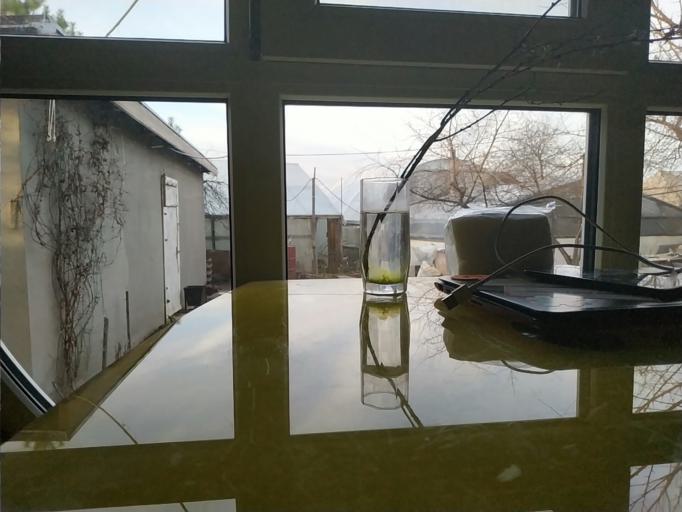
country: RU
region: Republic of Karelia
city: Suoyarvi
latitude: 62.2569
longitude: 32.0923
